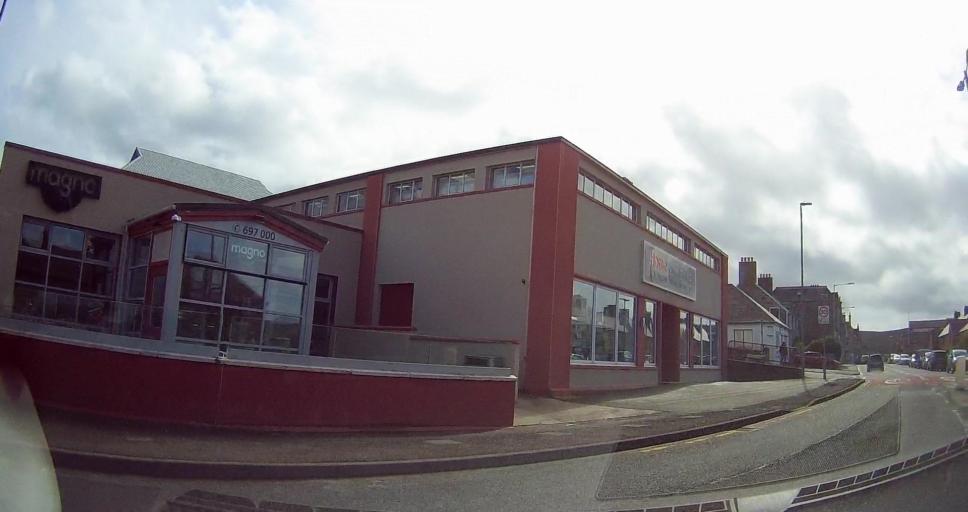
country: GB
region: Scotland
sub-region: Shetland Islands
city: Shetland
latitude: 60.1579
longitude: -1.1463
